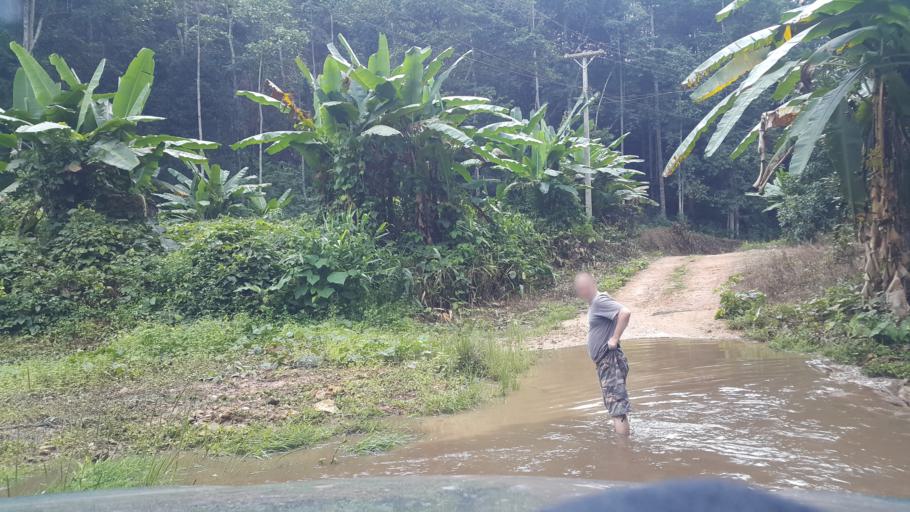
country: TH
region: Chiang Mai
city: Phrao
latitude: 19.1103
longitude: 99.2881
